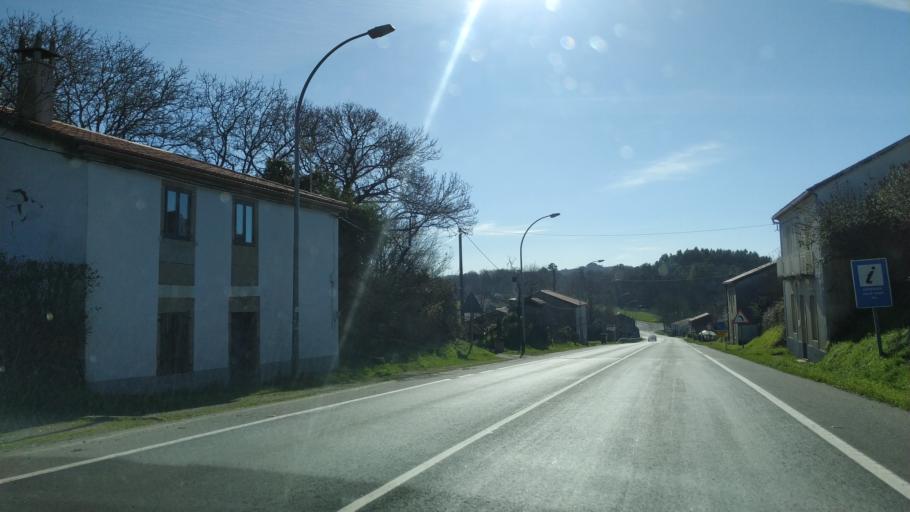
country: ES
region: Galicia
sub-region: Provincia de Pontevedra
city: Lalin
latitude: 42.6780
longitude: -8.1656
